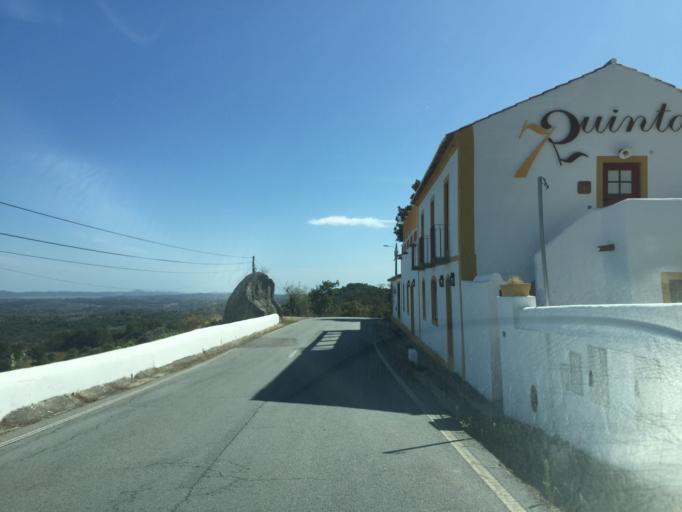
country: PT
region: Portalegre
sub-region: Marvao
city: Marvao
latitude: 39.4017
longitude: -7.3771
